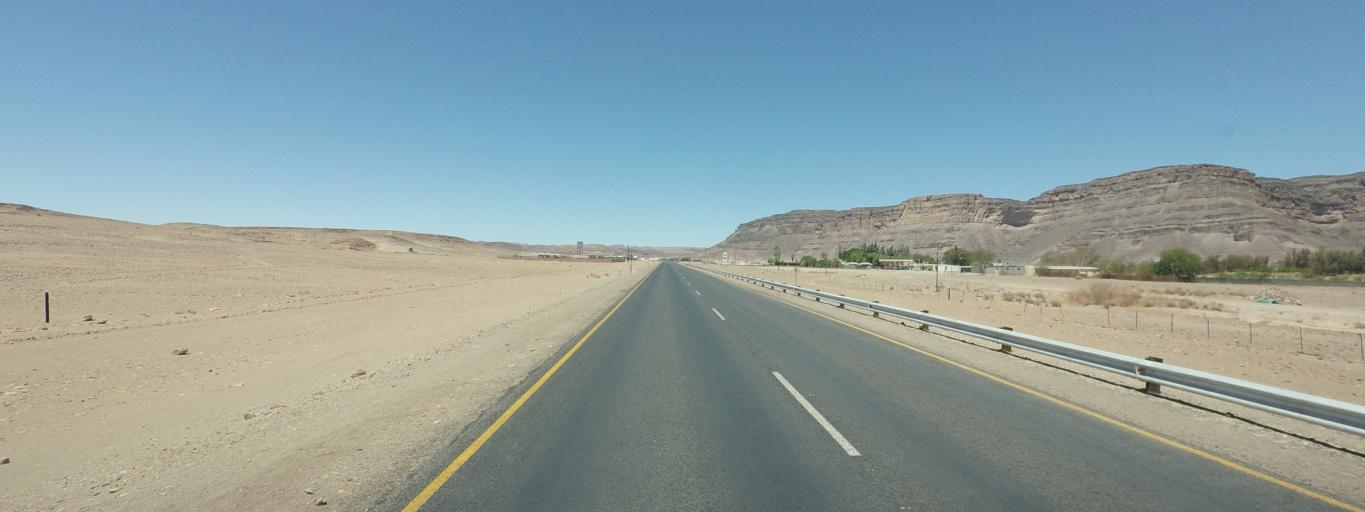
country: ZA
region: Northern Cape
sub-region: Namakwa District Municipality
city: Port Nolloth
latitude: -28.7406
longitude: 17.6176
